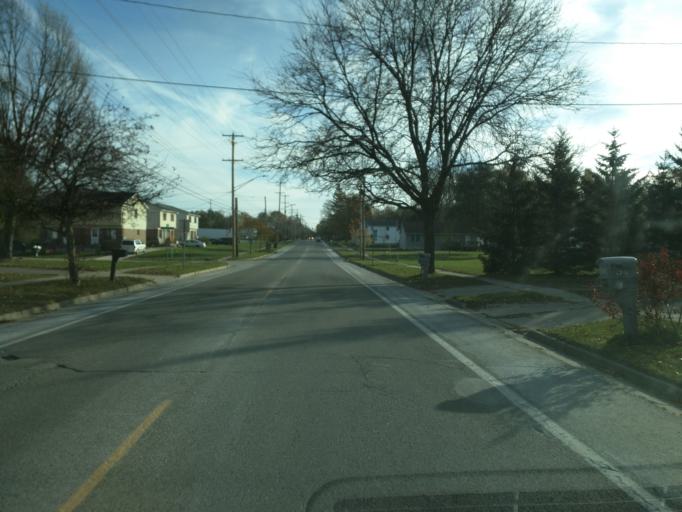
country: US
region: Michigan
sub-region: Ingham County
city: Holt
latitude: 42.6693
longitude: -84.5662
